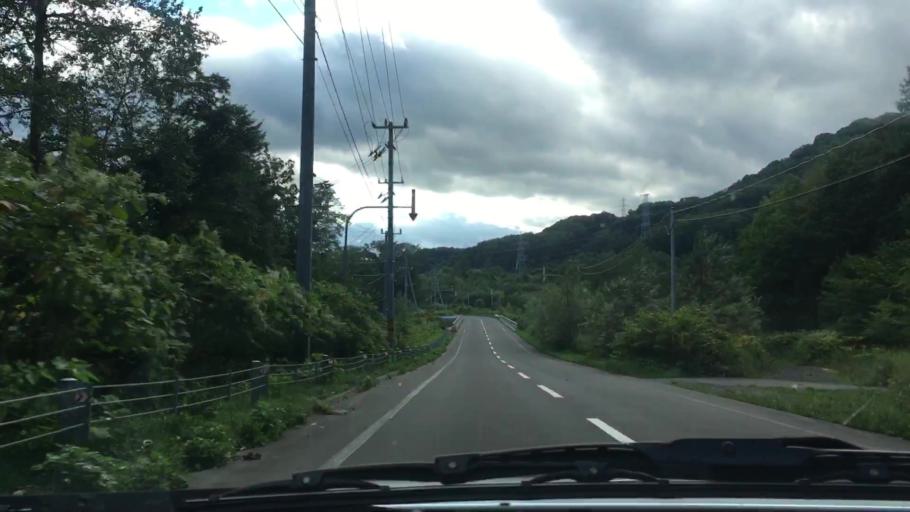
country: JP
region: Hokkaido
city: Otofuke
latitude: 43.1685
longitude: 142.9100
